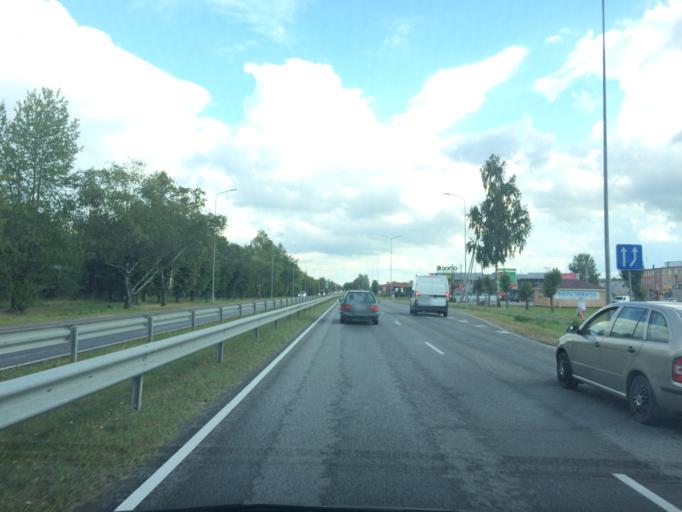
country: LV
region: Ogre
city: Ogre
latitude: 56.7974
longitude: 24.6237
